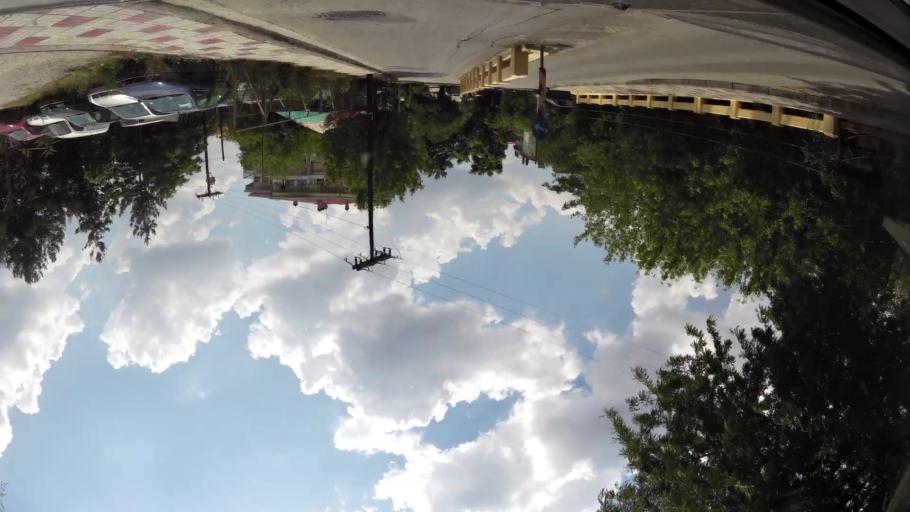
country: GR
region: West Macedonia
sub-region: Nomos Kozanis
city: Kozani
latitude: 40.2943
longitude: 21.7856
